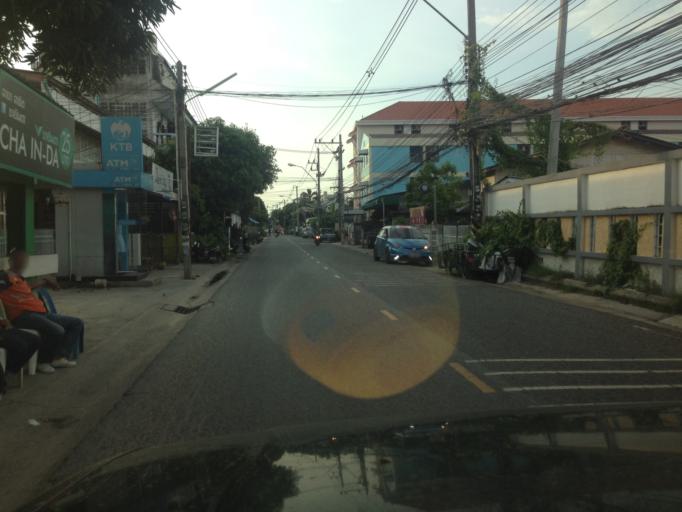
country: TH
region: Chon Buri
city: Si Racha
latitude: 13.2777
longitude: 100.9215
